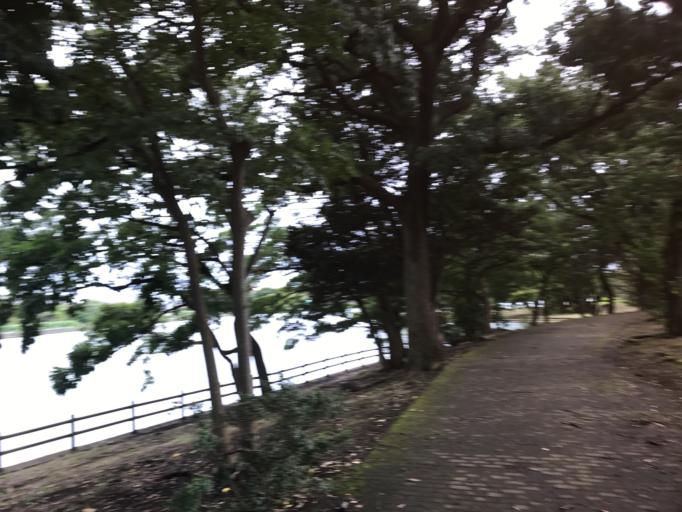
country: JP
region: Shizuoka
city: Numazu
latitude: 35.1290
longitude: 138.8835
